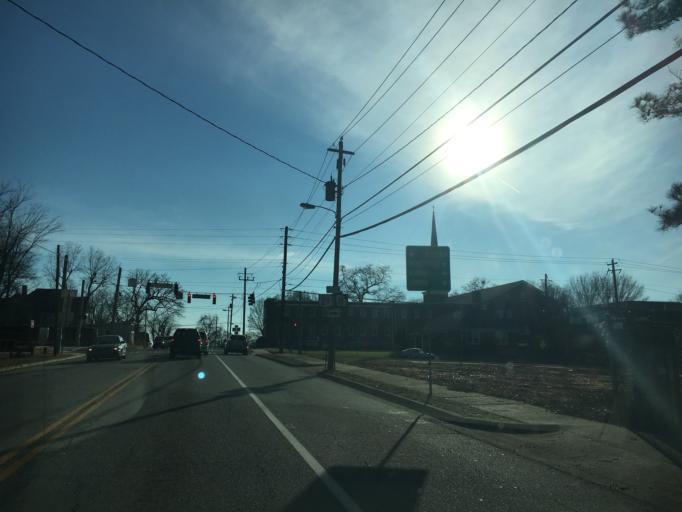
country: US
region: Georgia
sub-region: Hart County
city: Hartwell
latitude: 34.3549
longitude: -82.9361
